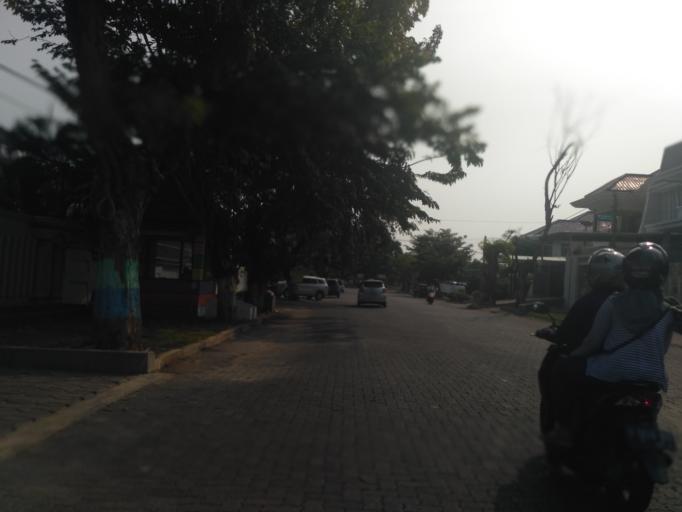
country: ID
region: Central Java
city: Semarang
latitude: -6.9678
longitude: 110.3877
